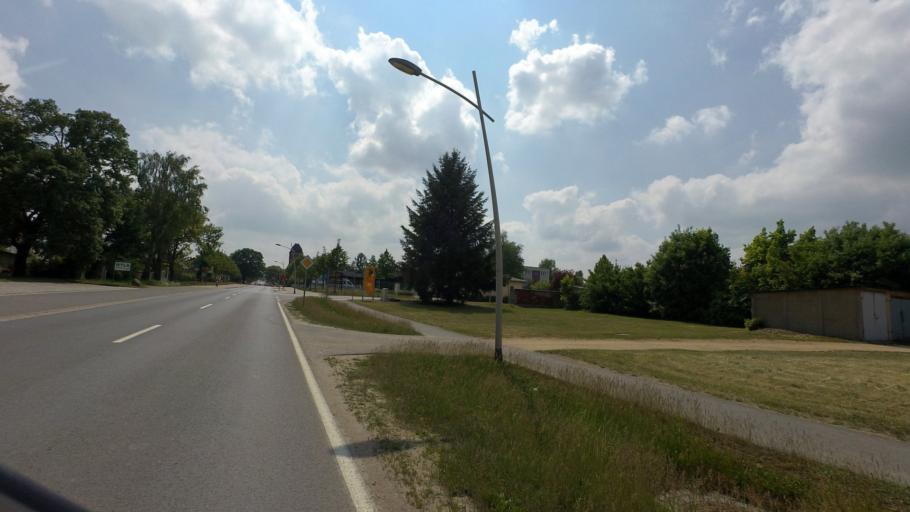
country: DE
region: Saxony
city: Niesky
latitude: 51.3017
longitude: 14.8272
